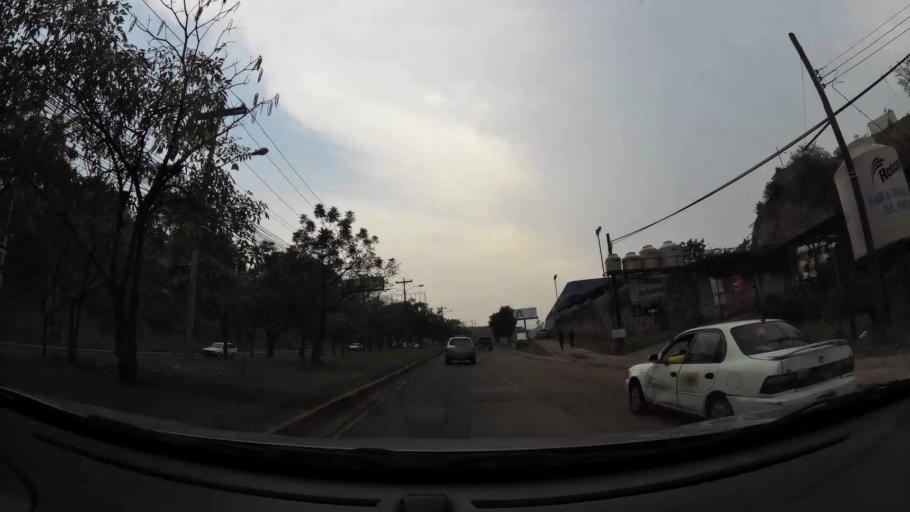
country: HN
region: Francisco Morazan
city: El Tablon
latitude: 14.0465
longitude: -87.1843
